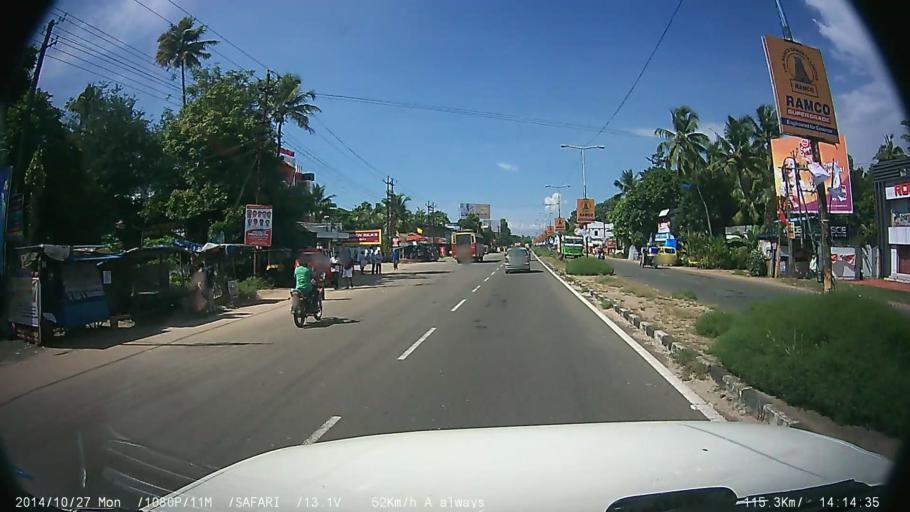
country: IN
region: Kerala
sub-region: Alappuzha
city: Kutiatodu
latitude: 9.8246
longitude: 76.3108
